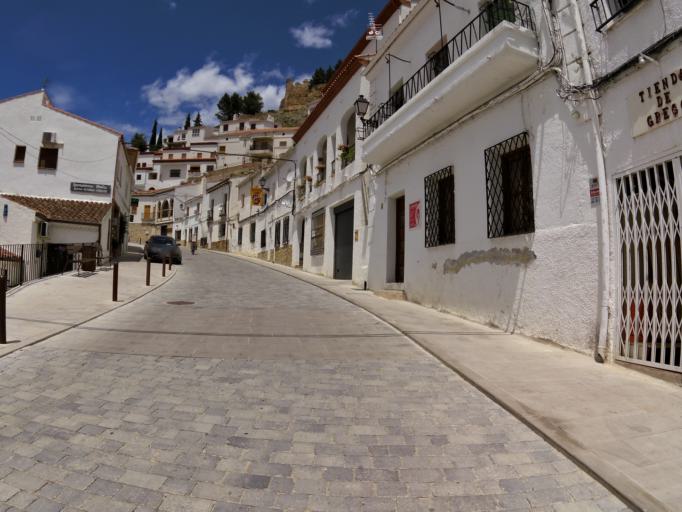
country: ES
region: Andalusia
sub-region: Provincia de Jaen
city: Segura de la Sierra
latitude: 38.2970
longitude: -2.6507
